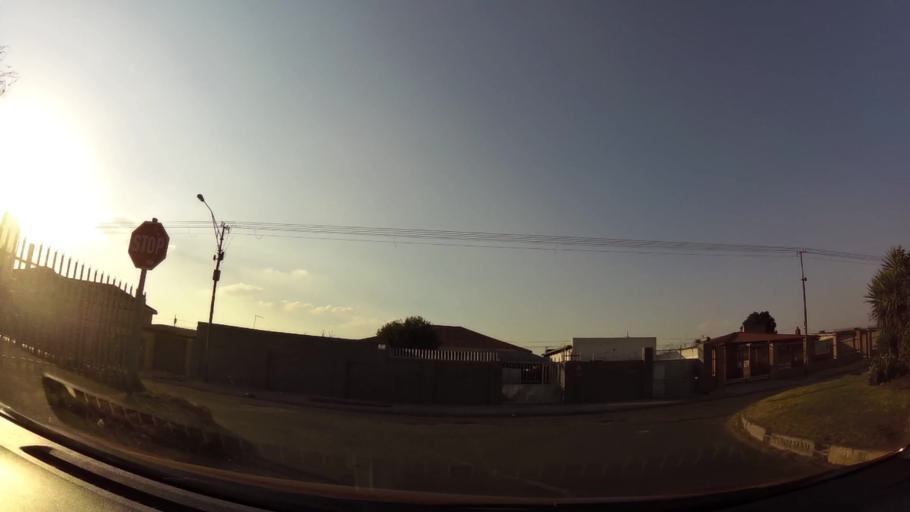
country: ZA
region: Gauteng
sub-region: City of Johannesburg Metropolitan Municipality
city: Soweto
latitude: -26.2854
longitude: 27.8946
